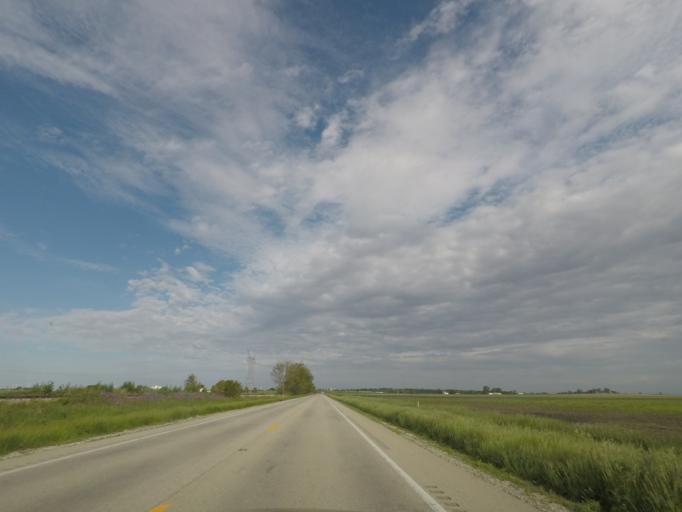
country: US
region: Illinois
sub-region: Logan County
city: Mount Pulaski
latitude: 39.9956
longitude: -89.2564
